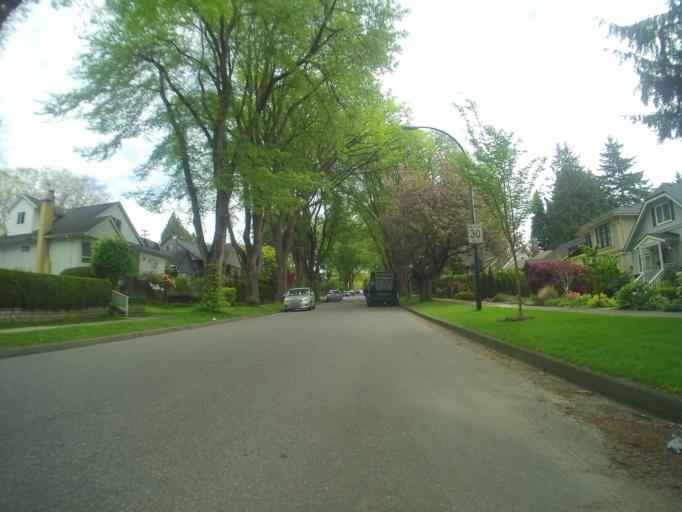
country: CA
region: British Columbia
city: West End
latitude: 49.2462
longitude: -123.1879
